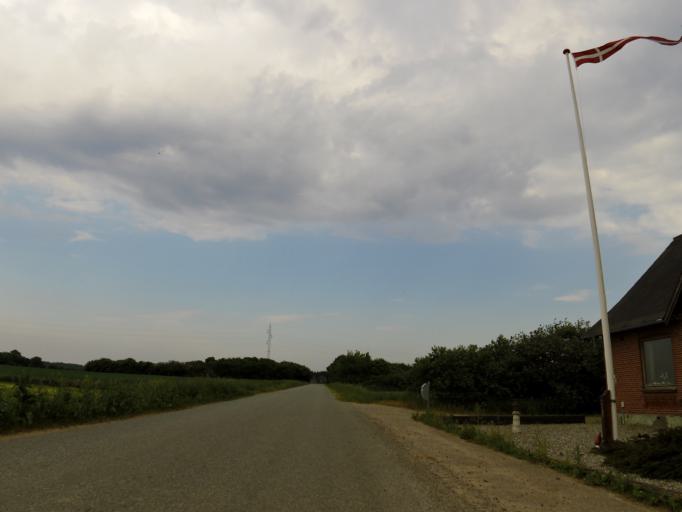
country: DK
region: Central Jutland
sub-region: Holstebro Kommune
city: Vinderup
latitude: 56.4978
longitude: 8.7816
